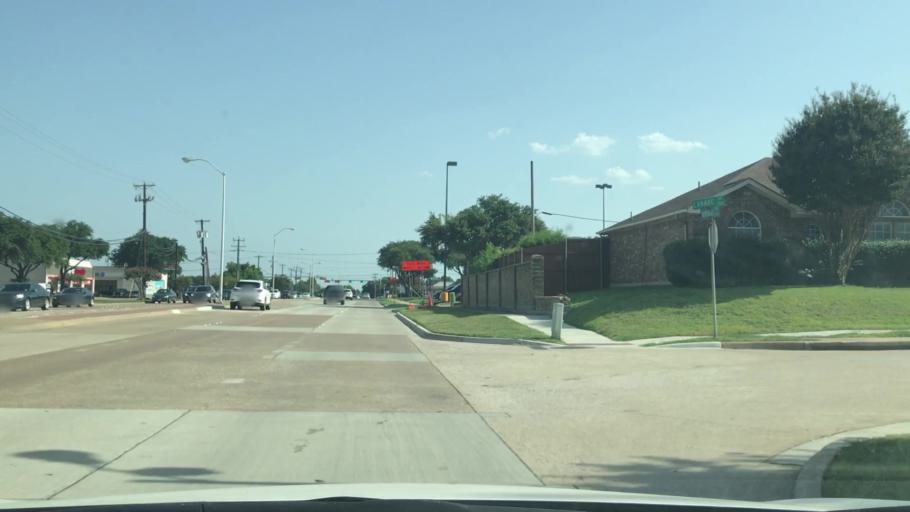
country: US
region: Texas
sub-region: Collin County
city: Plano
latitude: 33.0434
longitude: -96.7534
